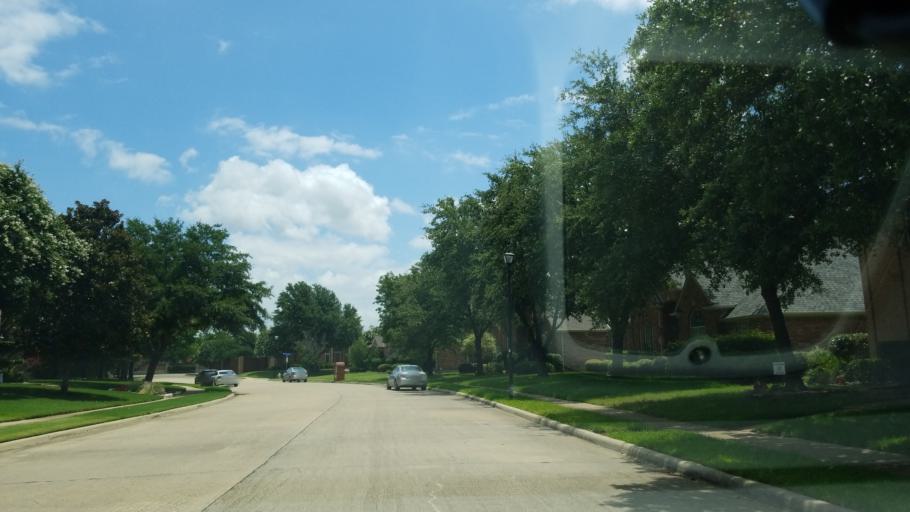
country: US
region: Texas
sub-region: Dallas County
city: Carrollton
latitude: 32.9581
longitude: -96.9511
